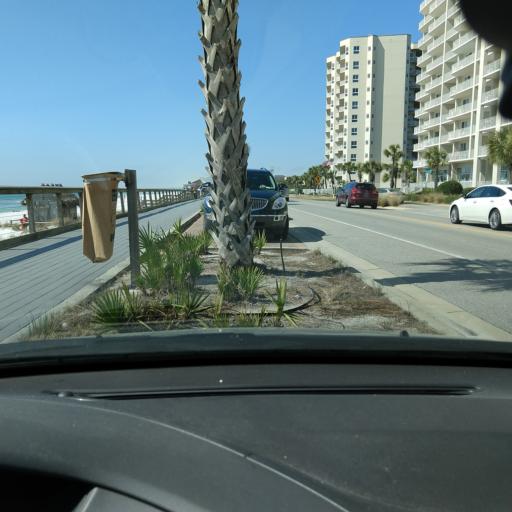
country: US
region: Florida
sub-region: Walton County
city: Miramar Beach
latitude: 30.3756
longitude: -86.3684
